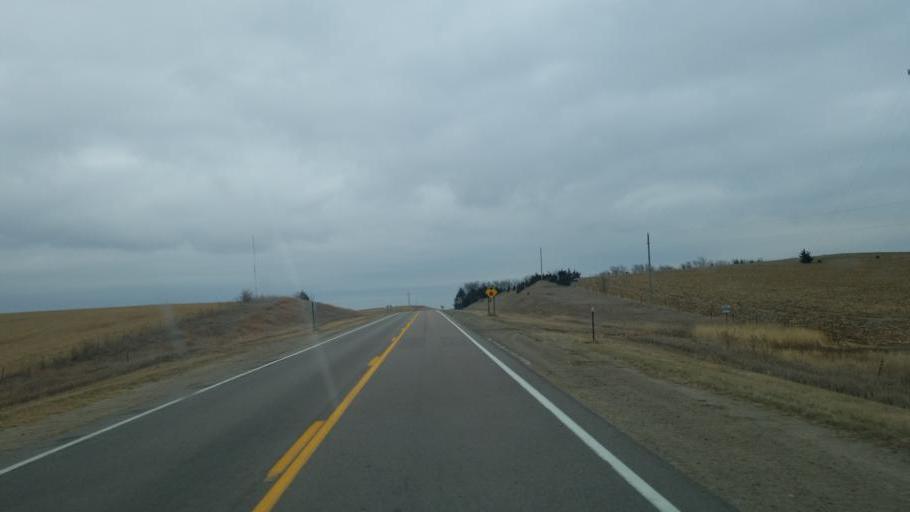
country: US
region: South Dakota
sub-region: Yankton County
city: Yankton
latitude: 42.7287
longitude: -97.4141
